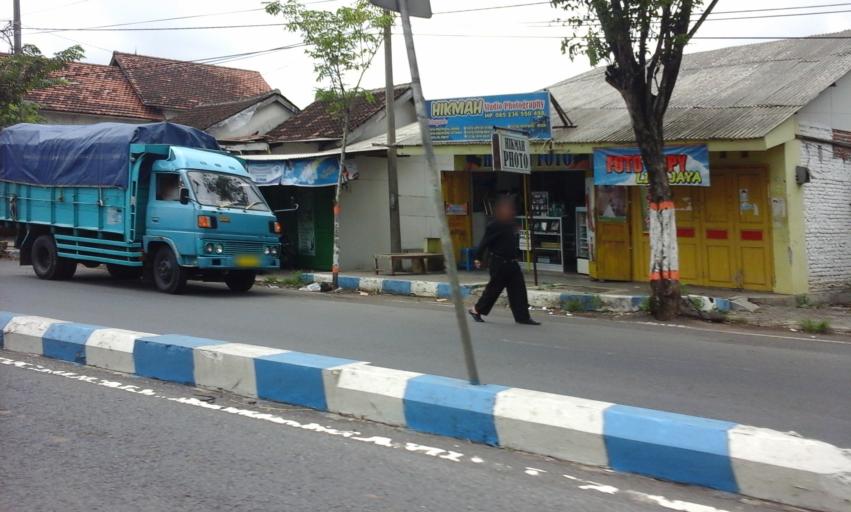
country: ID
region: East Java
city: Krajan
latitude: -8.0737
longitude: 113.2365
